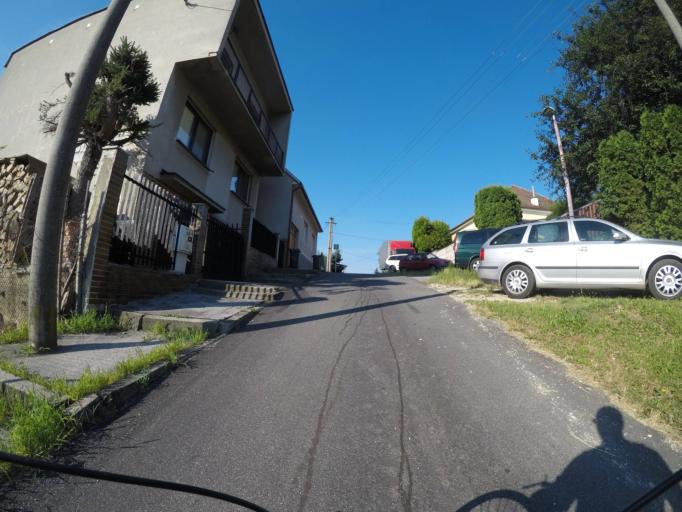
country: SK
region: Trenciansky
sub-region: Okres Nove Mesto nad Vahom
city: Nove Mesto nad Vahom
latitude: 48.7656
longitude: 17.8310
